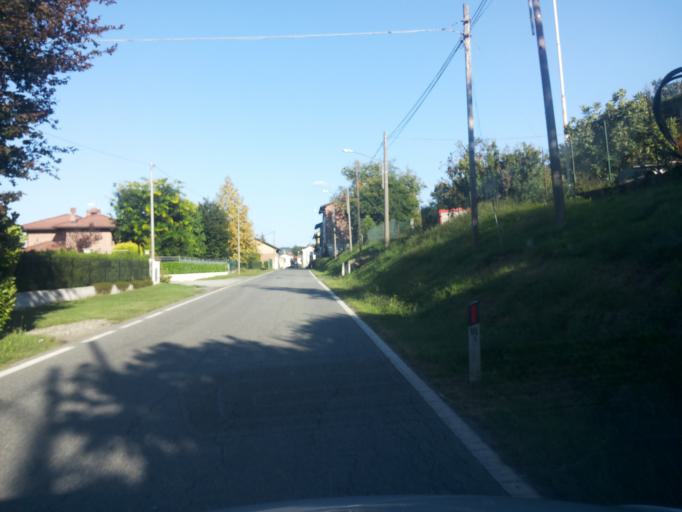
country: IT
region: Piedmont
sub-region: Provincia di Torino
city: Caravino
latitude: 45.3980
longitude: 7.9534
